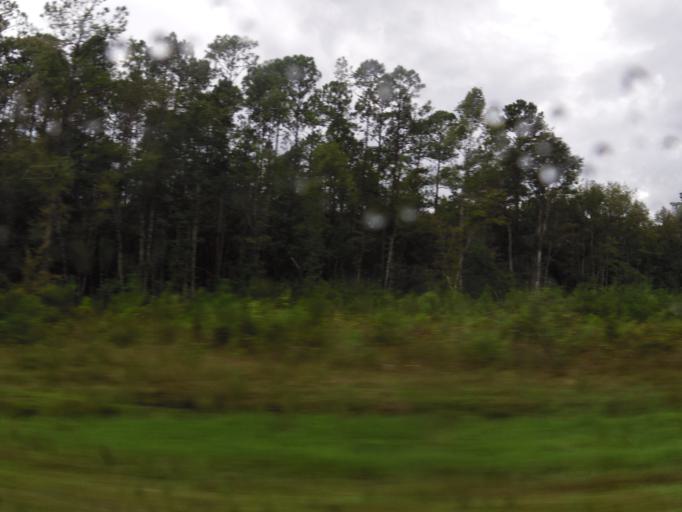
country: US
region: Florida
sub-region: Duval County
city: Baldwin
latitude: 30.4822
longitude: -81.9986
